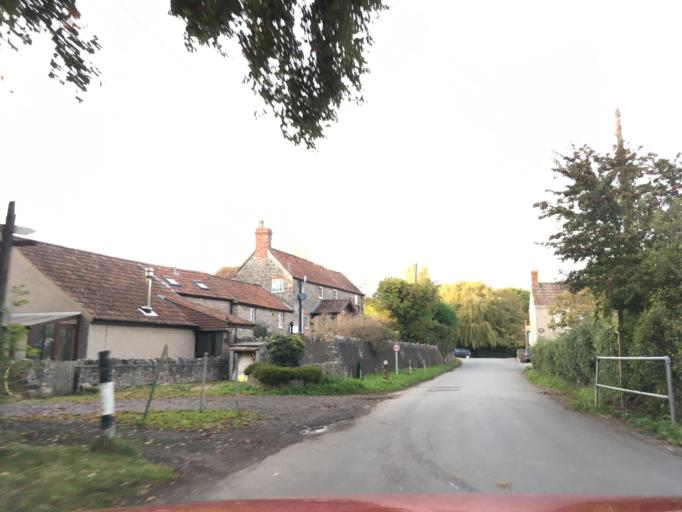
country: GB
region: England
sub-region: South Gloucestershire
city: Thornbury
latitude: 51.6283
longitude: -2.5668
